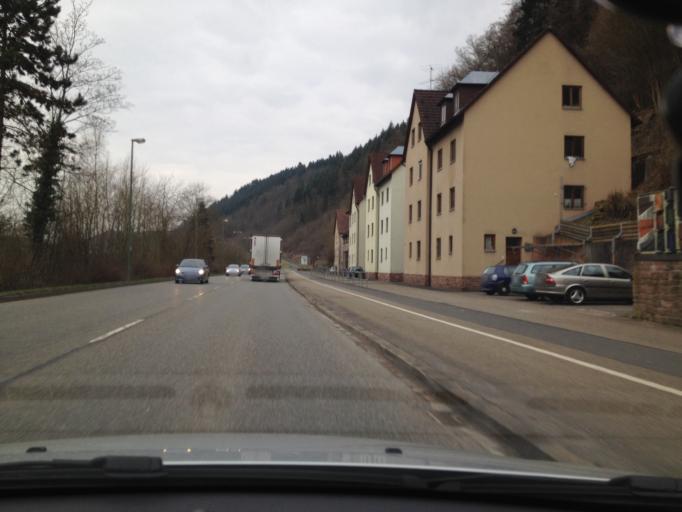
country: DE
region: Bavaria
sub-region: Regierungsbezirk Unterfranken
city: Kreuzwertheim
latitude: 49.7742
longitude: 9.5087
